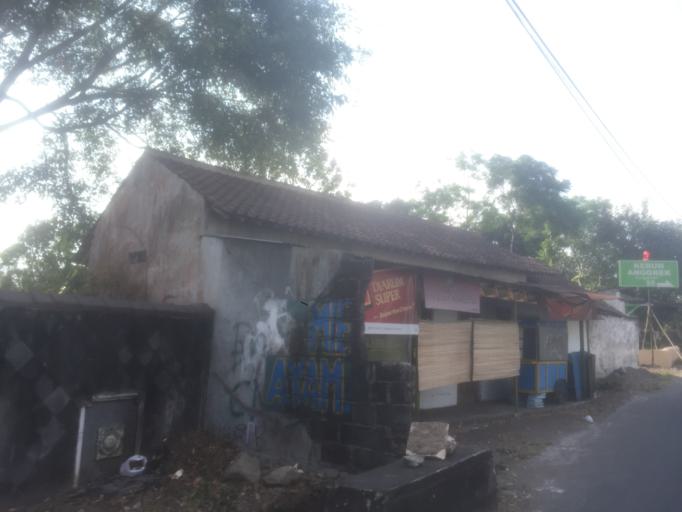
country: ID
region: Daerah Istimewa Yogyakarta
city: Sleman
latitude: -7.6752
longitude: 110.4173
